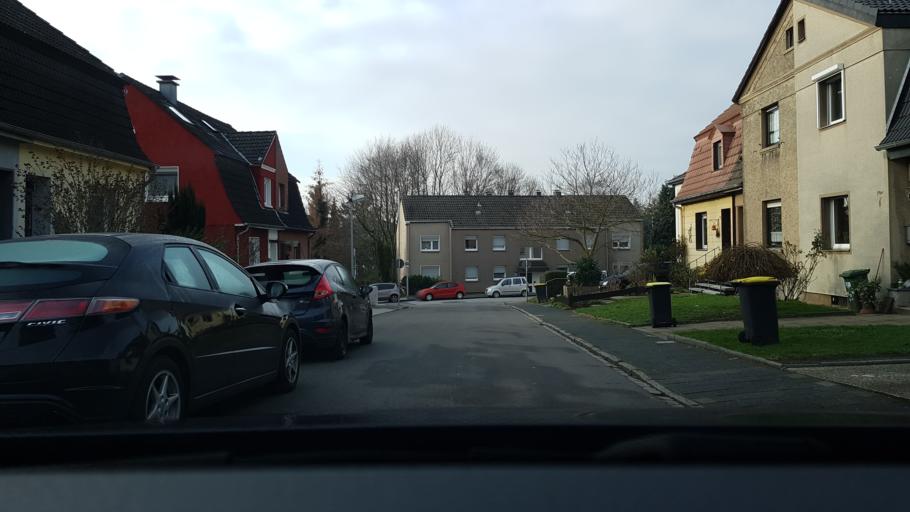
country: DE
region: North Rhine-Westphalia
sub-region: Regierungsbezirk Dusseldorf
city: Muelheim (Ruhr)
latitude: 51.4366
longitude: 6.9143
